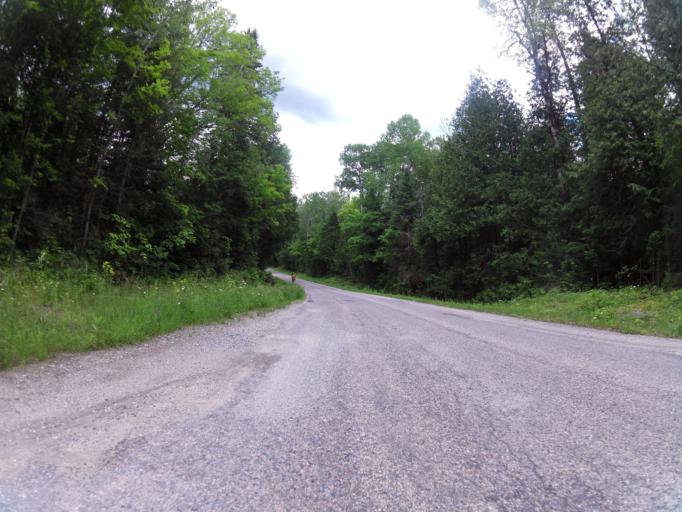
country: CA
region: Ontario
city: Renfrew
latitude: 45.0320
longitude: -76.7372
